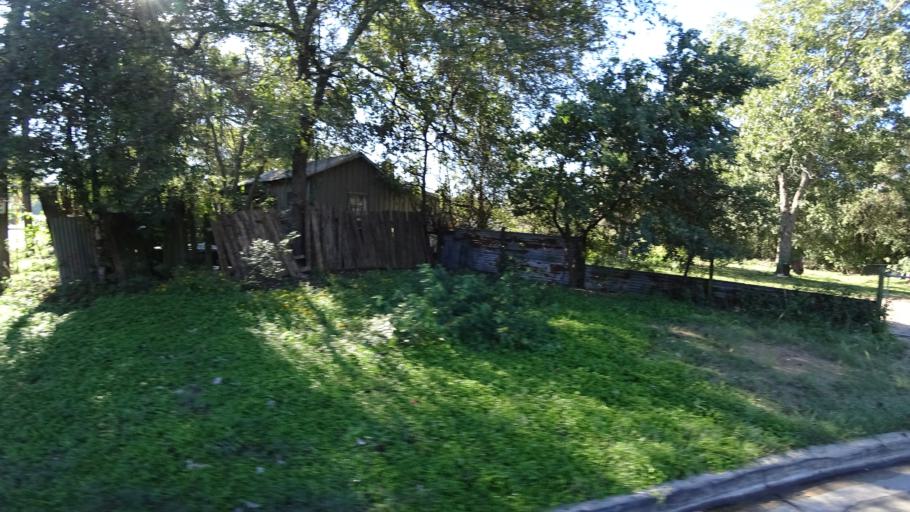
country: US
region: Texas
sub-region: Travis County
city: Austin
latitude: 30.2395
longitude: -97.6995
